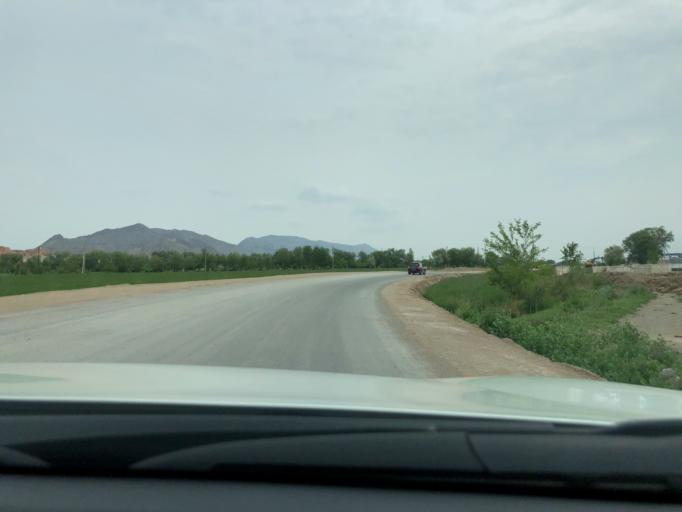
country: TJ
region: Viloyati Sughd
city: Isfara
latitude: 40.1520
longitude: 70.6197
